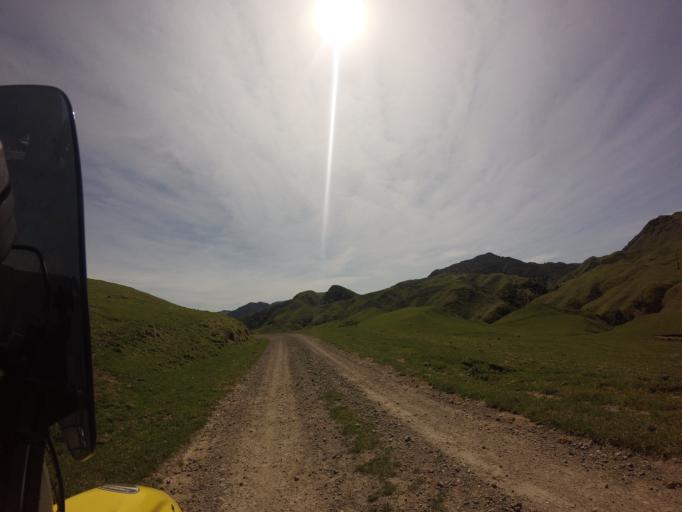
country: NZ
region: Bay of Plenty
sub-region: Opotiki District
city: Opotiki
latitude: -38.4554
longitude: 177.3713
